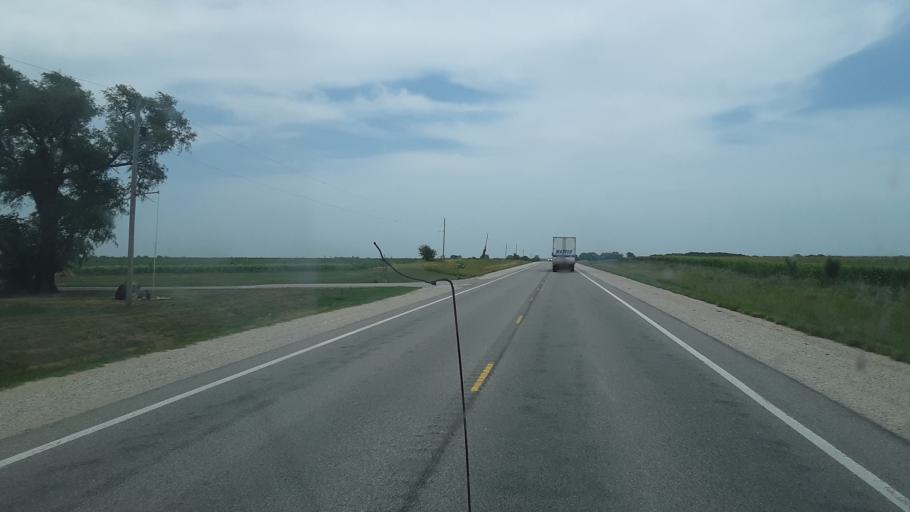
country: US
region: Kansas
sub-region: Allen County
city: Iola
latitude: 37.9218
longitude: -95.2718
